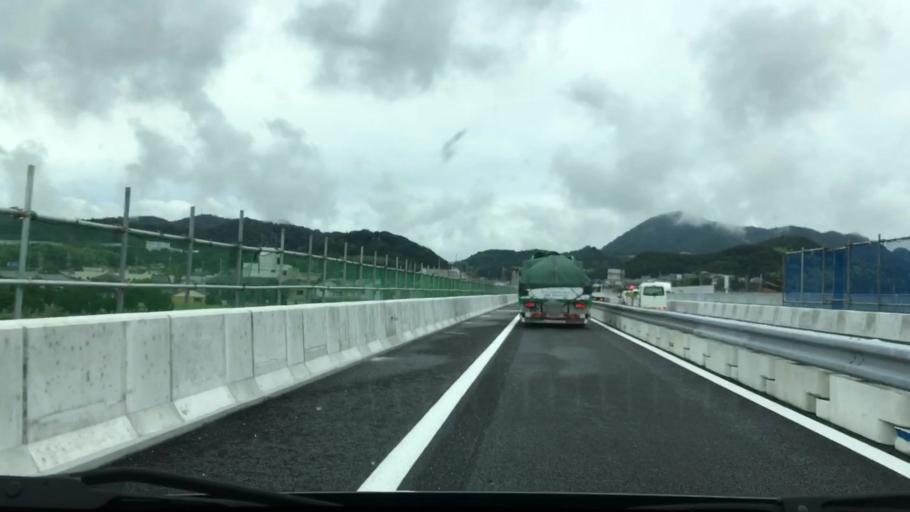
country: JP
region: Hyogo
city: Himeji
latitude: 34.9506
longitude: 134.7536
